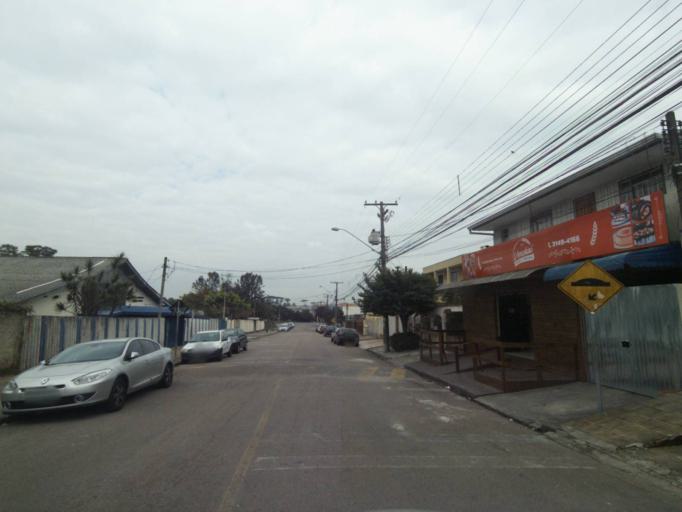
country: BR
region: Parana
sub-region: Curitiba
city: Curitiba
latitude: -25.5150
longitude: -49.3263
